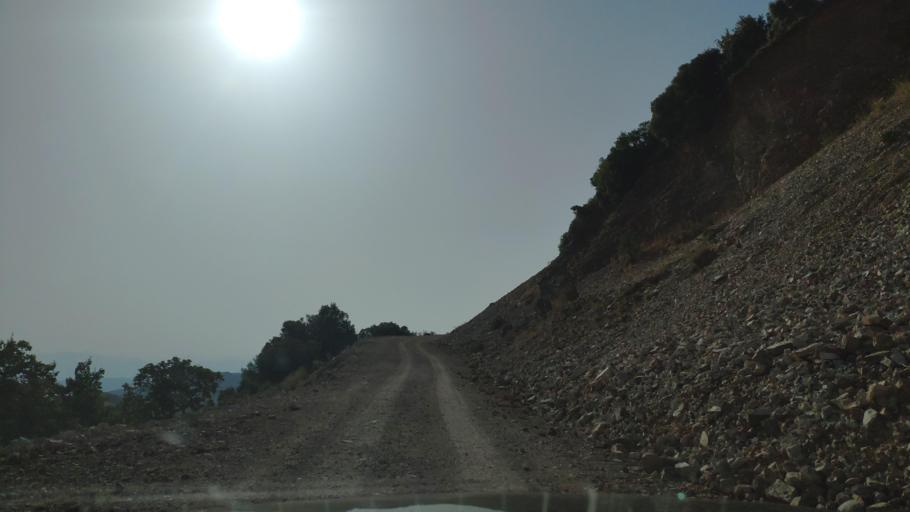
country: GR
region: West Greece
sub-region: Nomos Aitolias kai Akarnanias
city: Monastirakion
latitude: 38.8388
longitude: 20.9756
